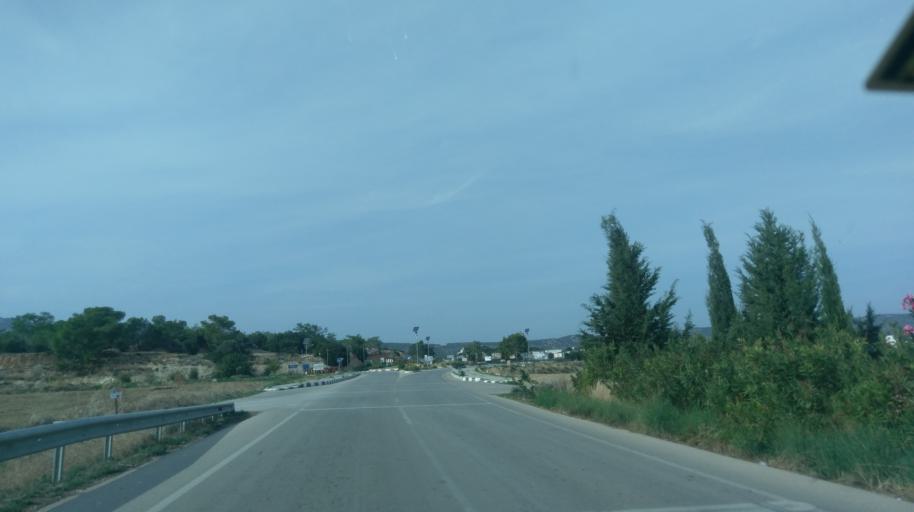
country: CY
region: Ammochostos
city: Trikomo
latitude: 35.4039
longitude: 33.9923
